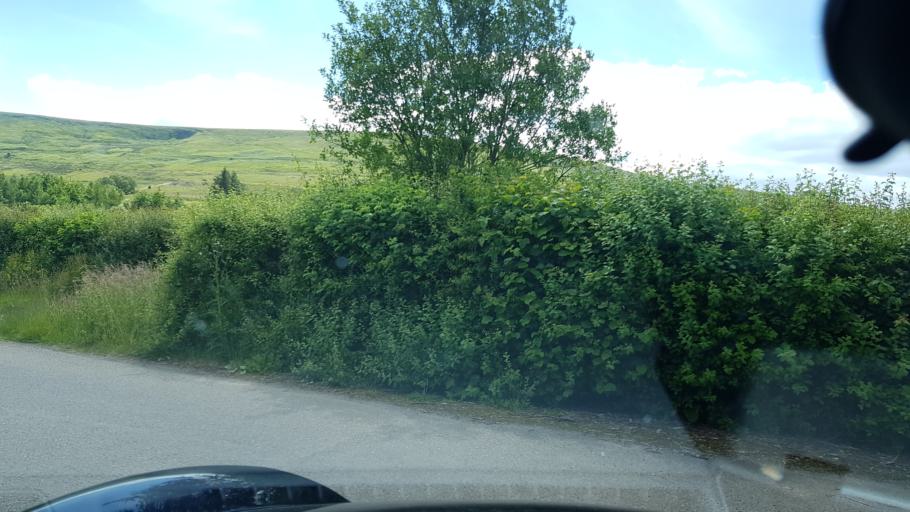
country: GB
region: Wales
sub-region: Torfaen County Borough
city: Blaenavon
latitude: 51.7823
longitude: -3.1117
